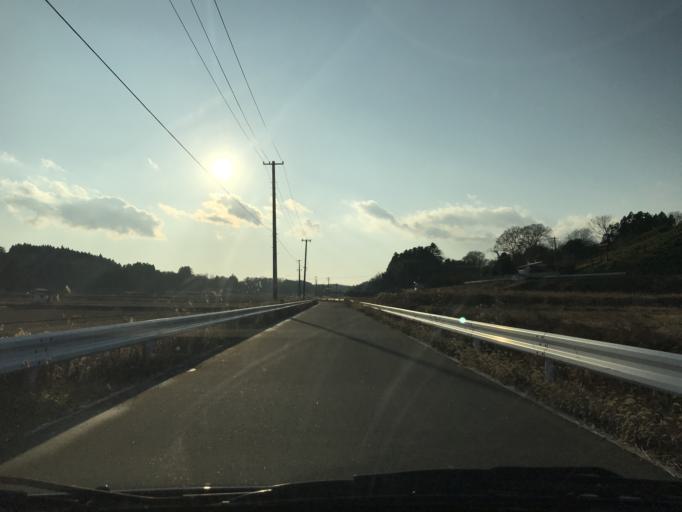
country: JP
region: Miyagi
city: Wakuya
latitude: 38.7031
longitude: 141.1211
